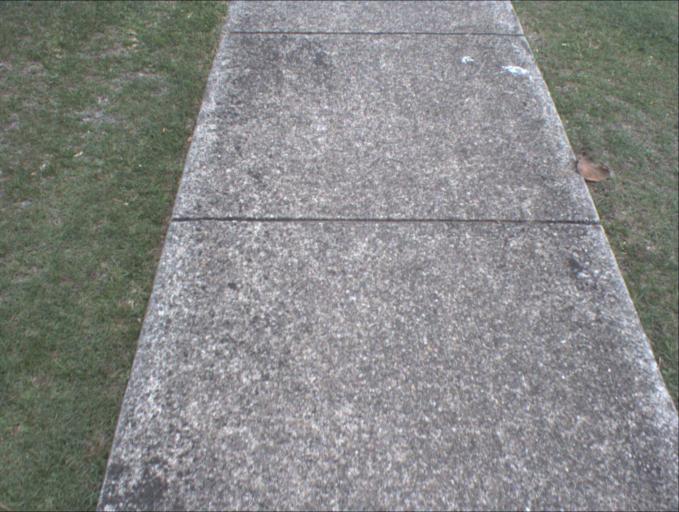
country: AU
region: Queensland
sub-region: Logan
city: Waterford West
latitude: -27.6894
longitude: 153.1034
